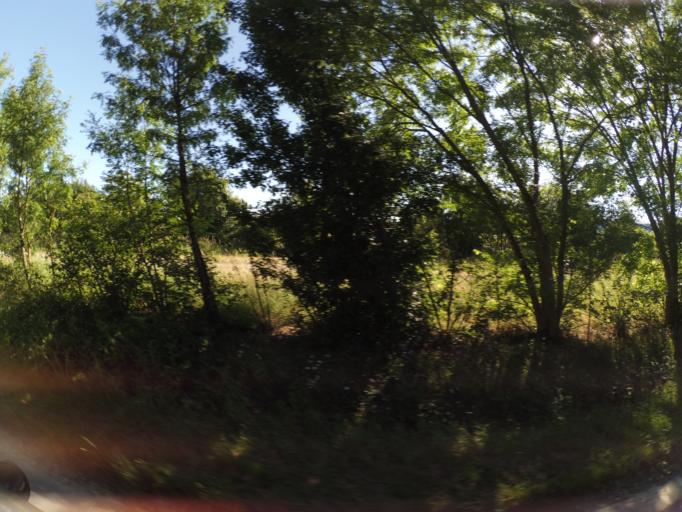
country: FR
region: Pays de la Loire
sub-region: Departement de la Vendee
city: Beaurepaire
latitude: 46.8988
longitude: -1.0672
